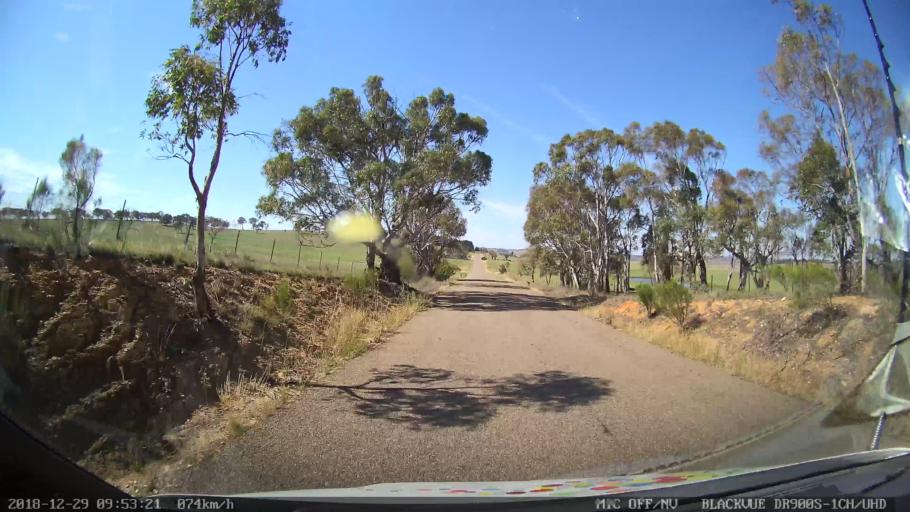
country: AU
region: New South Wales
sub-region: Goulburn Mulwaree
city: Goulburn
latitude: -34.7506
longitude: 149.4697
